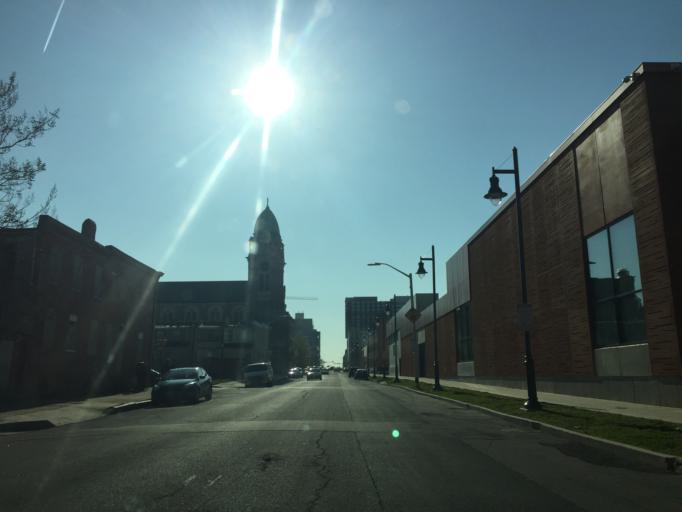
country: US
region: Maryland
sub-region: City of Baltimore
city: Baltimore
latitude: 39.3009
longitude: -76.5856
